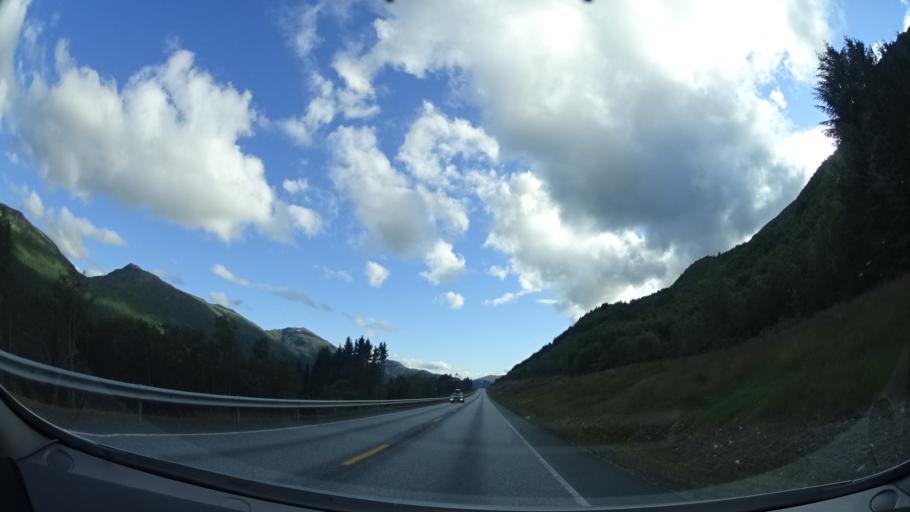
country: NO
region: More og Romsdal
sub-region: Gjemnes
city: Batnfjordsora
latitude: 62.9232
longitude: 7.7024
